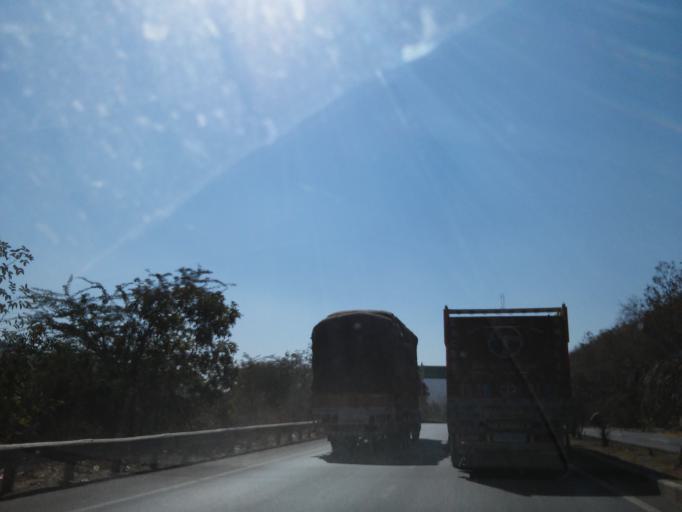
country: IN
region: Gujarat
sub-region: Sabar Kantha
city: Meghraj
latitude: 23.6947
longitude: 73.3873
